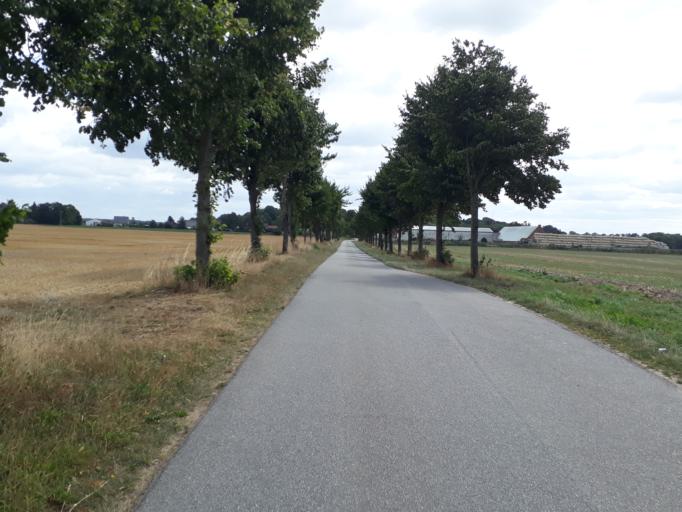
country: DE
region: Mecklenburg-Vorpommern
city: Marlow
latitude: 54.2286
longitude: 12.5461
